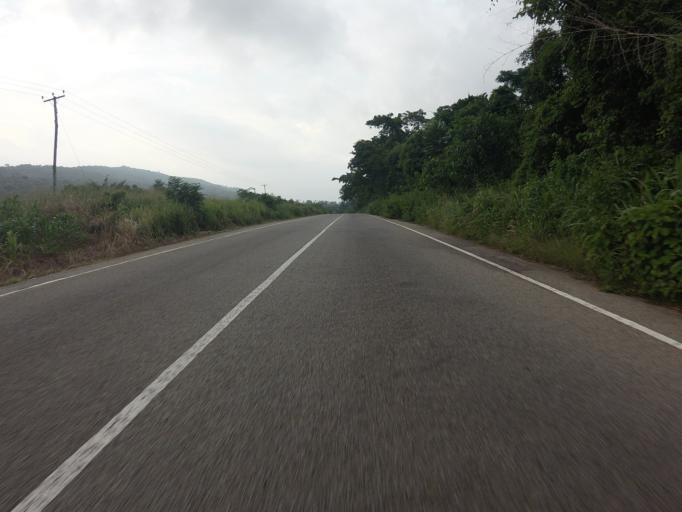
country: GH
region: Volta
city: Ho
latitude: 6.6449
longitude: 0.4695
